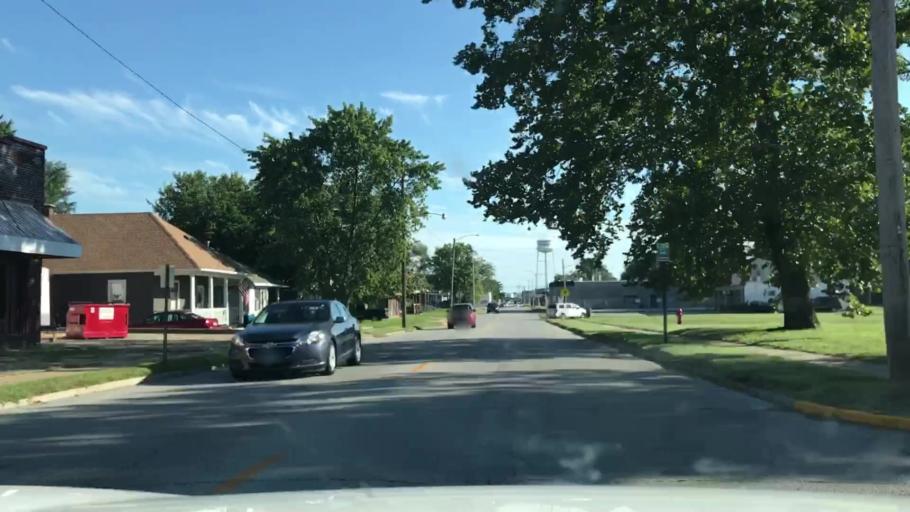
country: US
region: Illinois
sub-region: Madison County
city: Wood River
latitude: 38.8662
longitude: -90.0985
